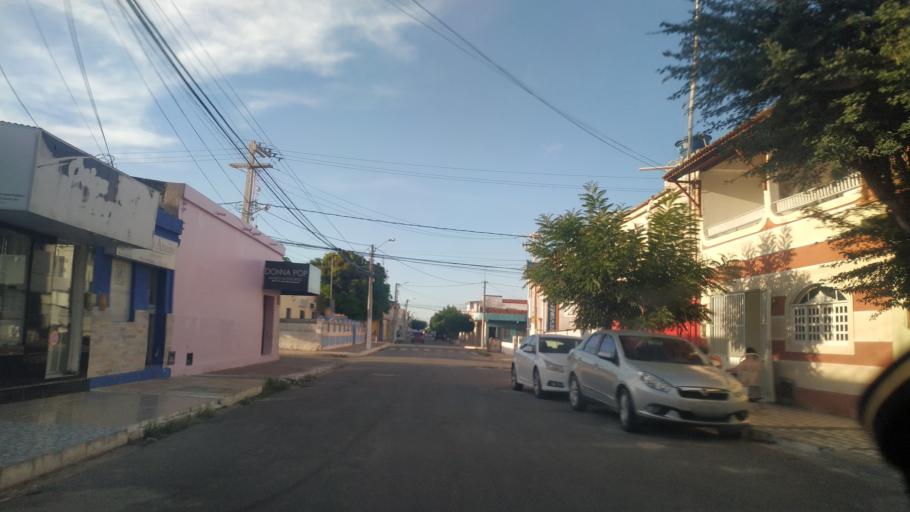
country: BR
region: Rio Grande do Norte
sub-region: Areia Branca
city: Areia Branca
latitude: -4.9574
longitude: -37.1345
